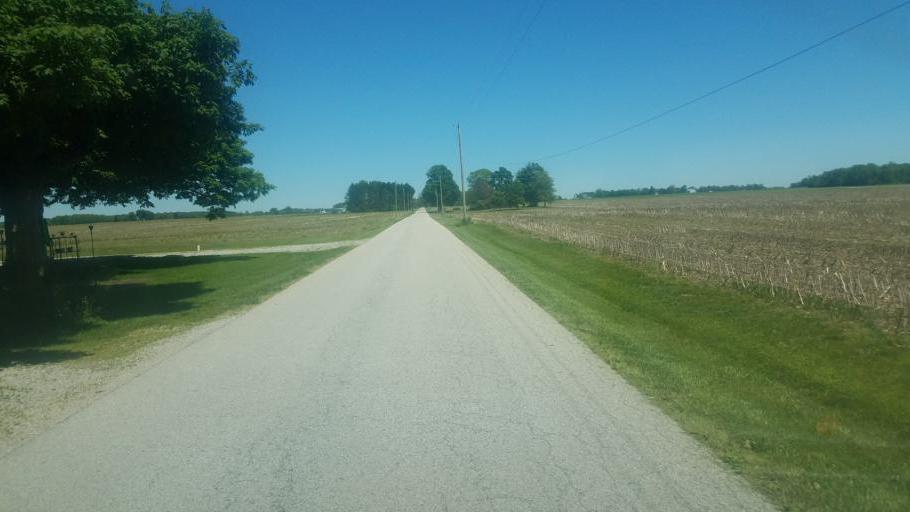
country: US
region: Ohio
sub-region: Champaign County
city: Saint Paris
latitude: 40.1996
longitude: -84.0488
